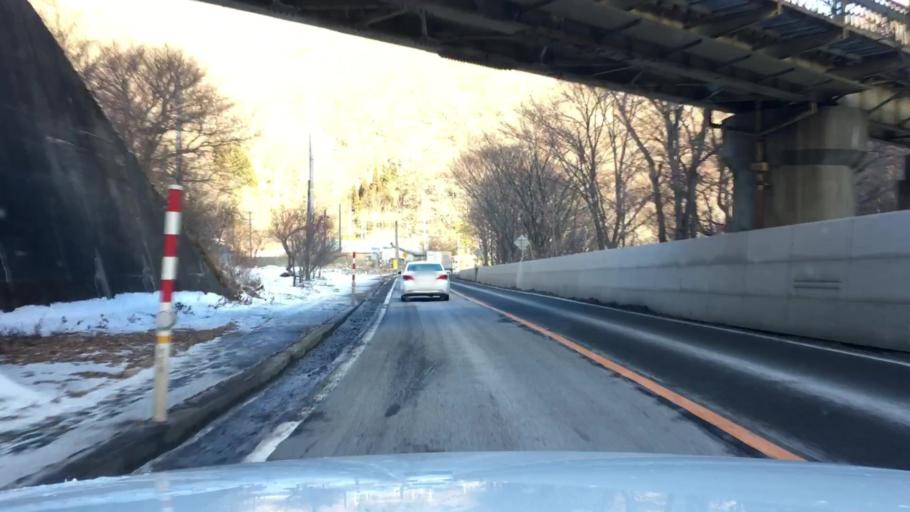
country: JP
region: Iwate
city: Tono
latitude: 39.6247
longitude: 141.5139
